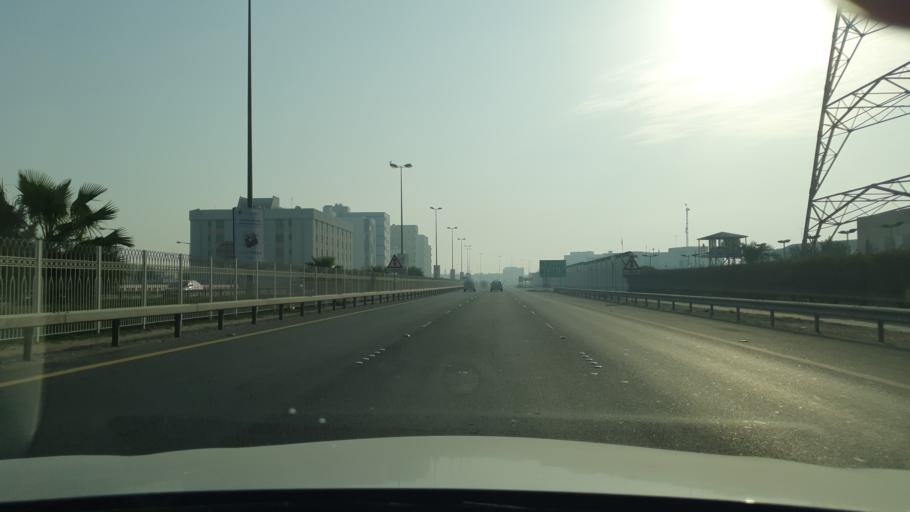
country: BH
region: Northern
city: Madinat `Isa
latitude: 26.1639
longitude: 50.5569
